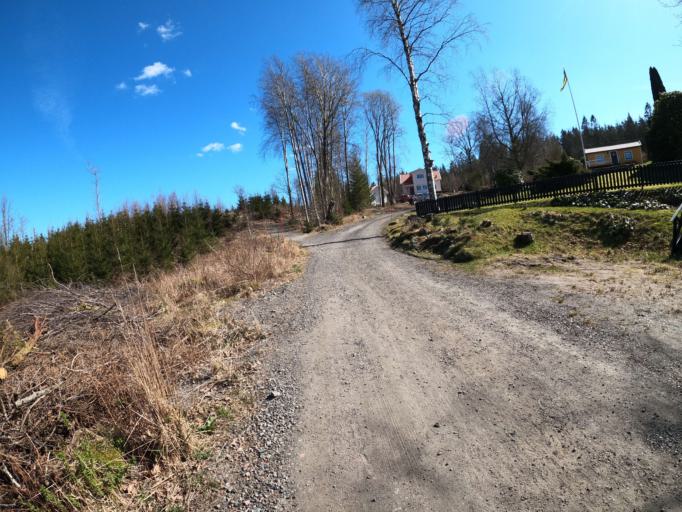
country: SE
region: Vaestra Goetaland
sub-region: Harryda Kommun
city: Molnlycke
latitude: 57.6297
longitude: 12.1252
